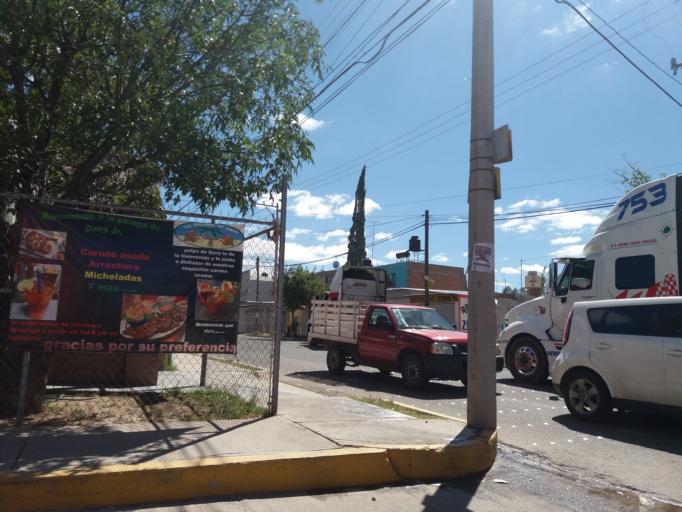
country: MX
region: Aguascalientes
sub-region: Aguascalientes
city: San Sebastian [Fraccionamiento]
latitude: 21.8008
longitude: -102.2758
